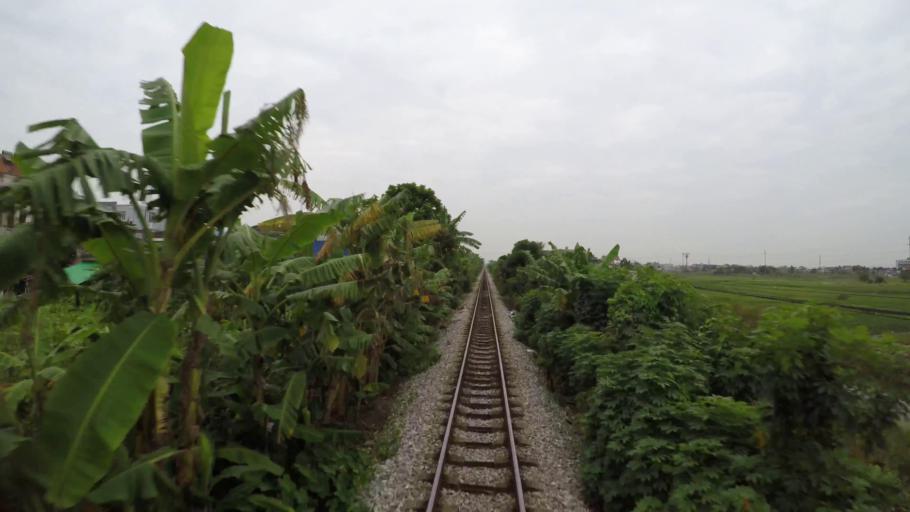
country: VN
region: Hai Phong
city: An Duong
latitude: 20.8944
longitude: 106.5879
